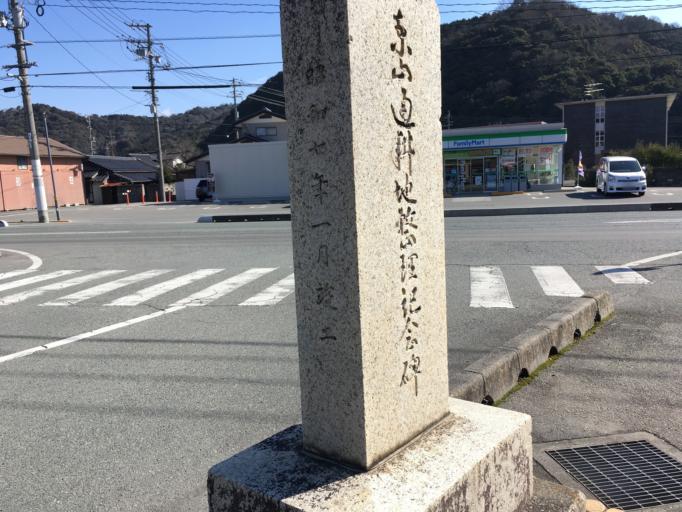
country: JP
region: Yamaguchi
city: Yamaguchi-shi
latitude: 34.1751
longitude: 131.4817
